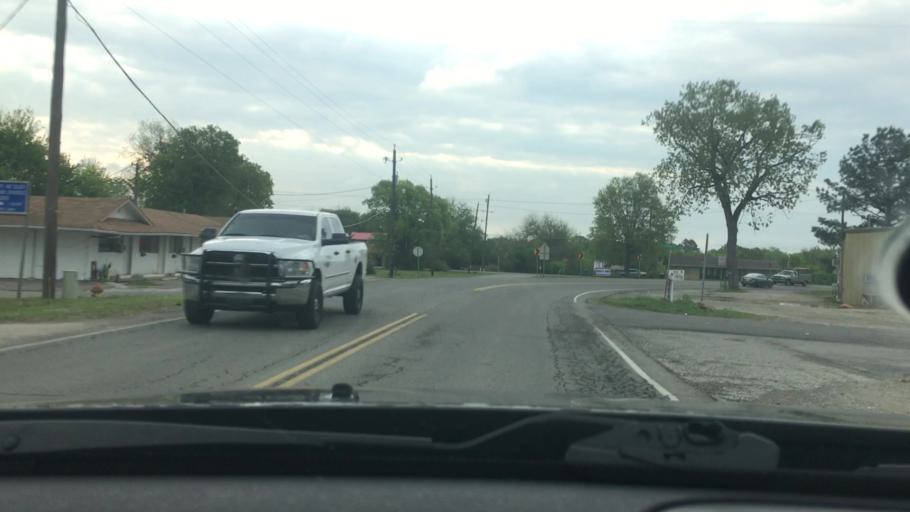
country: US
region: Oklahoma
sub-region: Coal County
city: Coalgate
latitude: 34.5365
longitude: -96.2177
